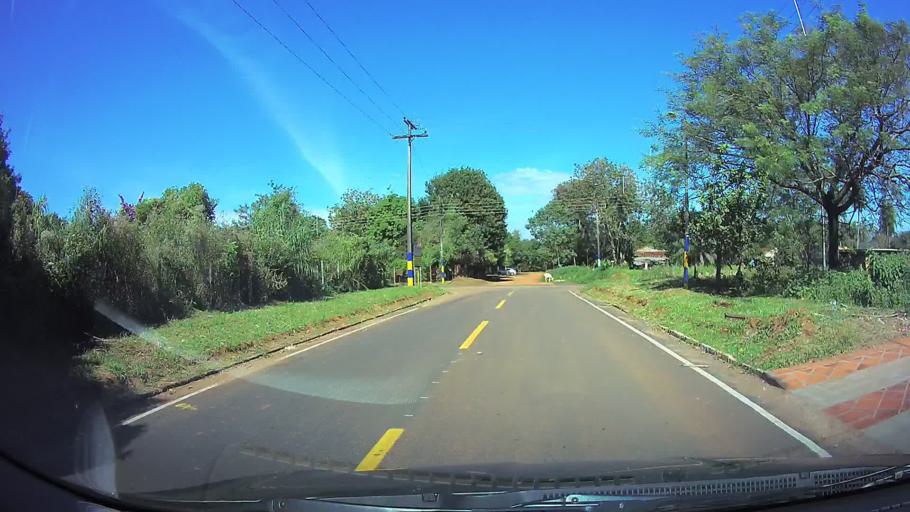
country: PY
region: Central
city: San Lorenzo
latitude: -25.2629
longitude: -57.4654
